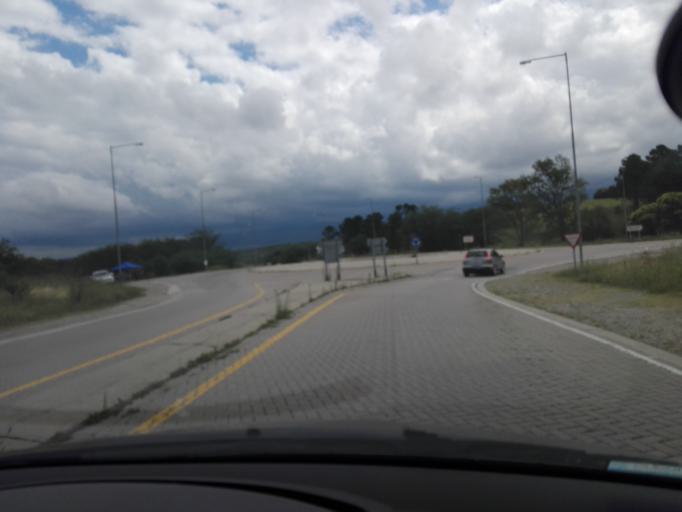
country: AR
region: Cordoba
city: Cuesta Blanca
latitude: -31.6066
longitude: -64.5601
